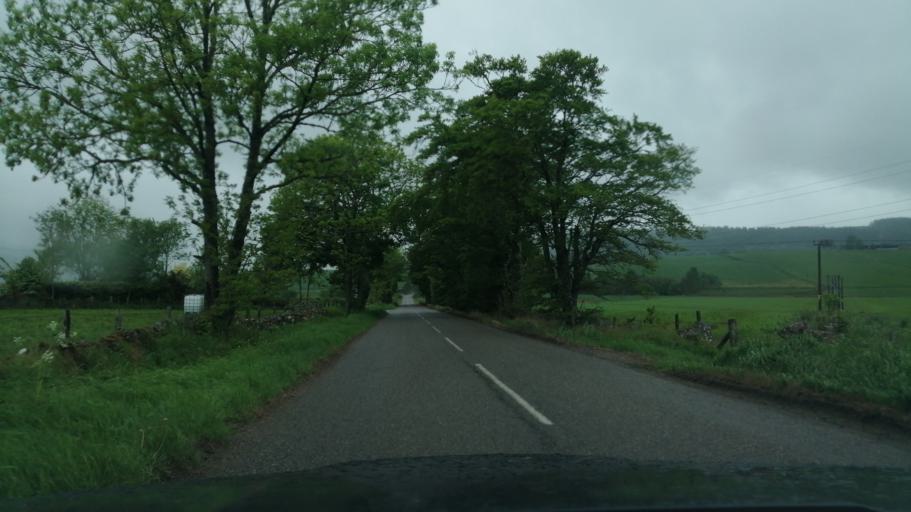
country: GB
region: Scotland
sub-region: Aberdeenshire
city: Huntly
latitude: 57.5430
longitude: -2.7983
